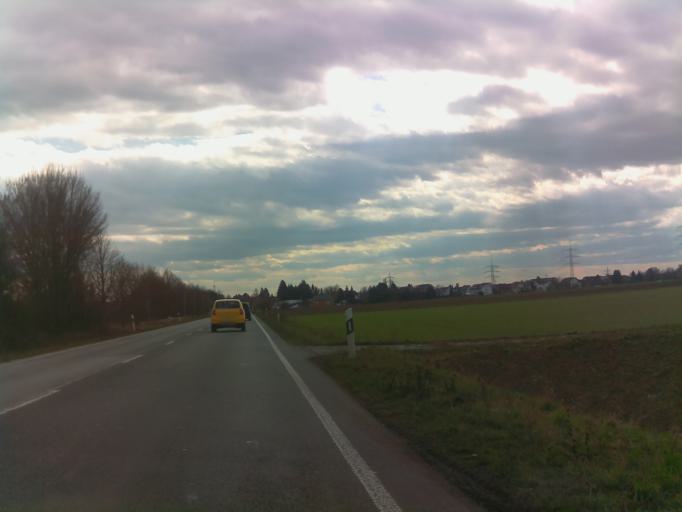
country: DE
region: Hesse
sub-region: Regierungsbezirk Darmstadt
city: Gross-Gerau
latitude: 49.8888
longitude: 8.4800
